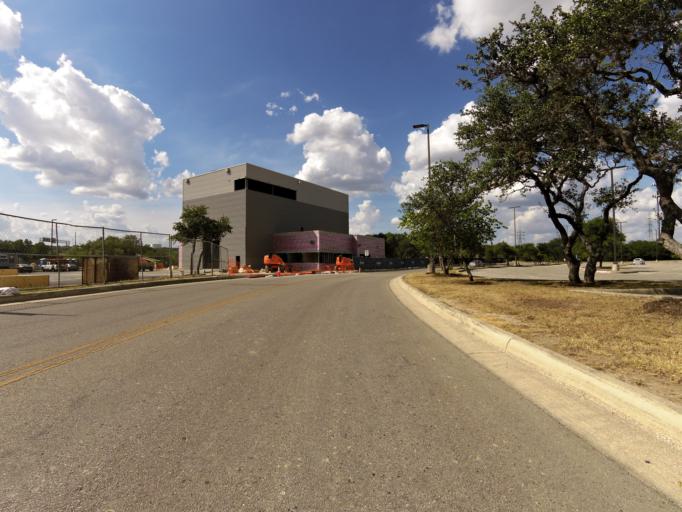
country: US
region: Texas
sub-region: Bexar County
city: Helotes
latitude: 29.5852
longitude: -98.6285
